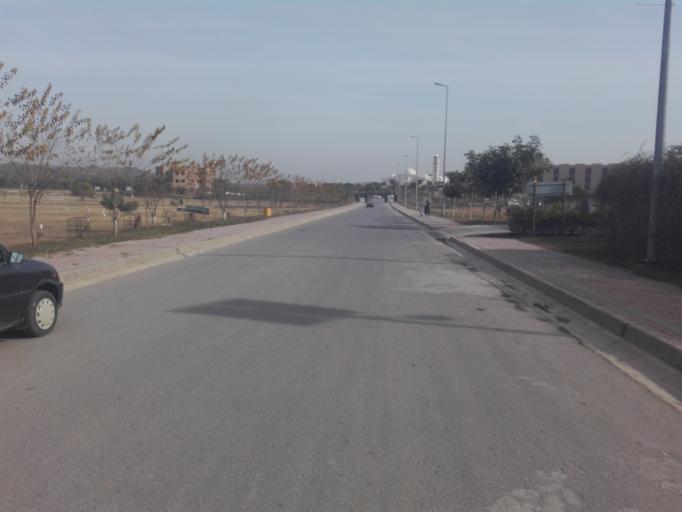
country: PK
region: Punjab
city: Rawalpindi
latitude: 33.6427
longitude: 72.9830
